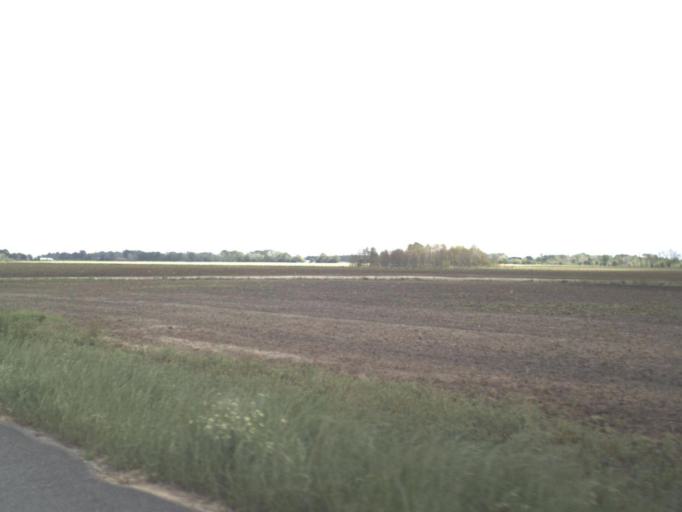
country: US
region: Florida
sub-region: Okaloosa County
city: Crestview
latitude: 30.8254
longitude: -86.6757
